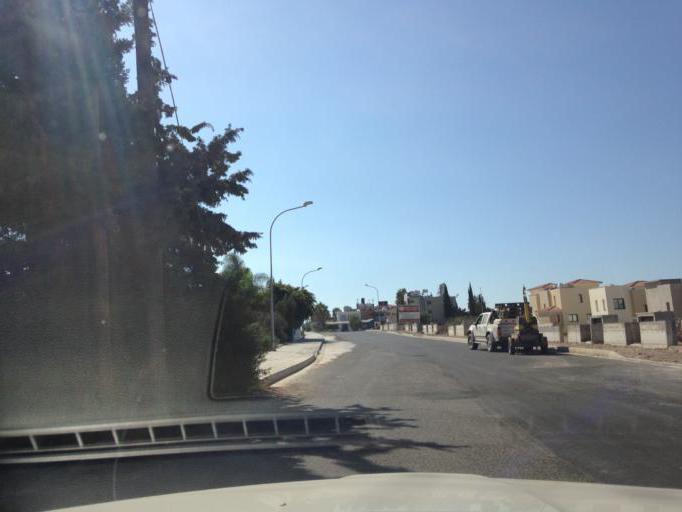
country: CY
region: Pafos
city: Pegeia
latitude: 34.8599
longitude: 32.3649
